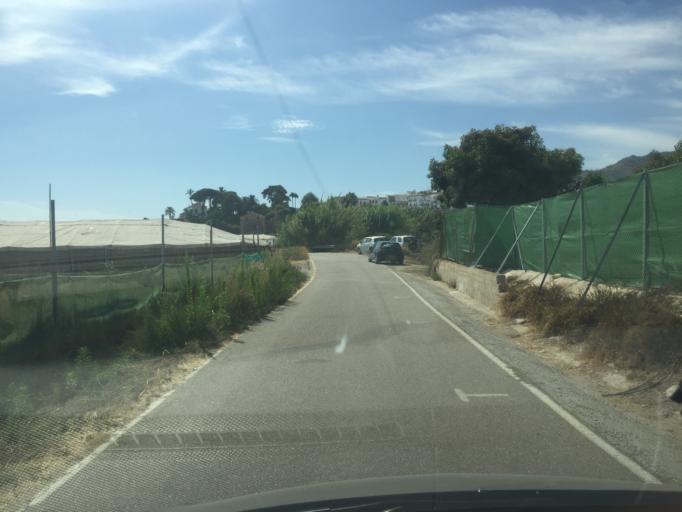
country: ES
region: Andalusia
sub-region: Provincia de Malaga
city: Nerja
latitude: 36.7559
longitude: -3.8393
